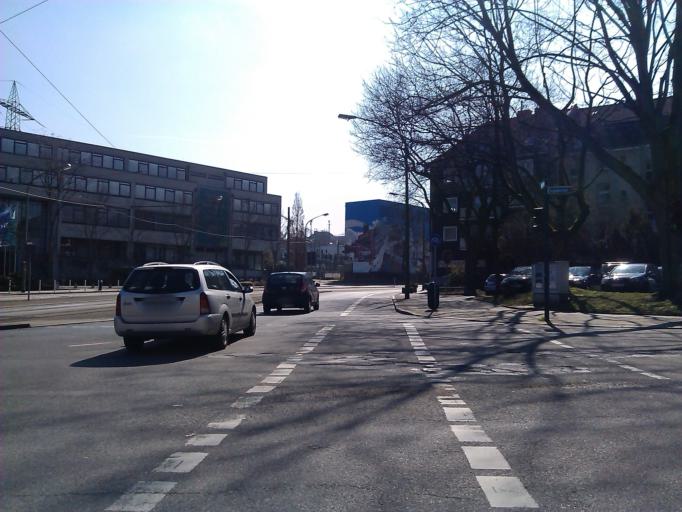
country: DE
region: North Rhine-Westphalia
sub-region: Regierungsbezirk Dusseldorf
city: Essen
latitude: 51.4574
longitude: 7.0223
